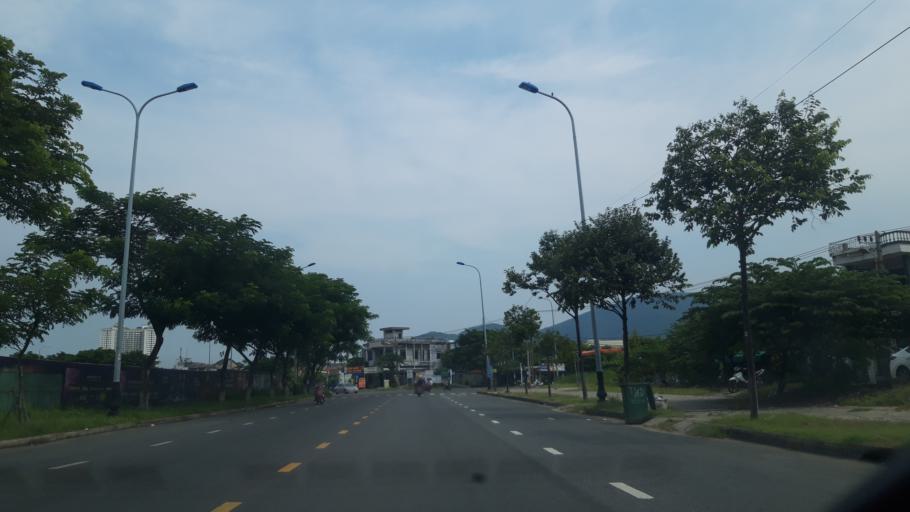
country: VN
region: Da Nang
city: Da Nang
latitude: 16.0875
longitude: 108.2289
